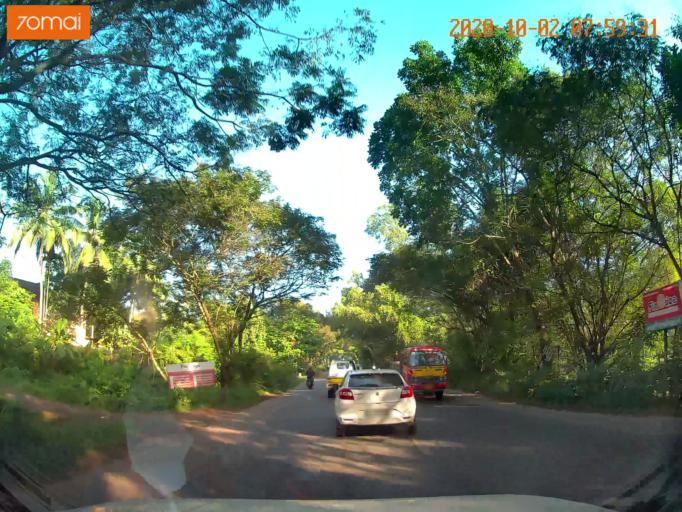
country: IN
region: Kerala
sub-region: Kozhikode
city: Ferokh
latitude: 11.2108
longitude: 75.8611
